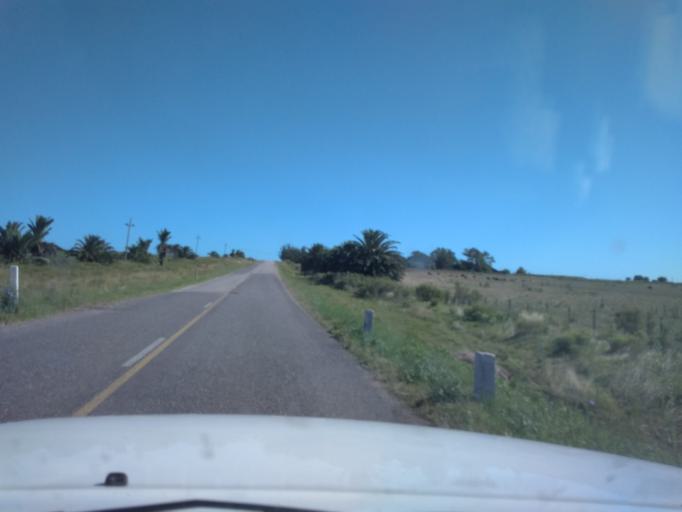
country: UY
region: Canelones
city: San Ramon
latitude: -34.1614
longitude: -55.9471
